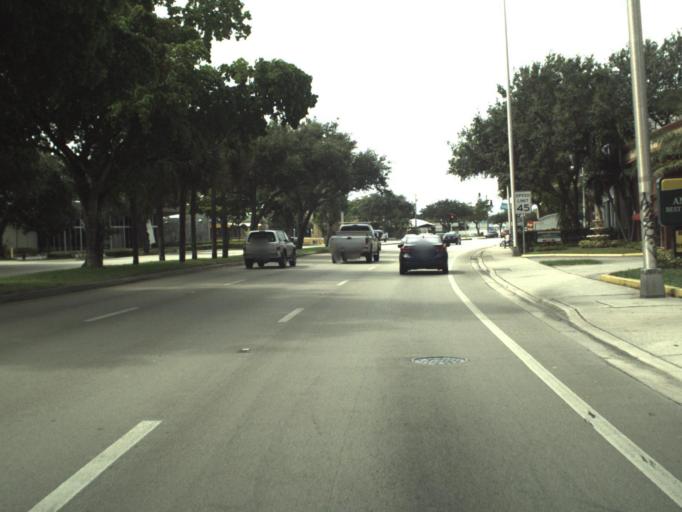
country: US
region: Florida
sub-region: Broward County
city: Oakland Park
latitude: 26.1647
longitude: -80.1159
